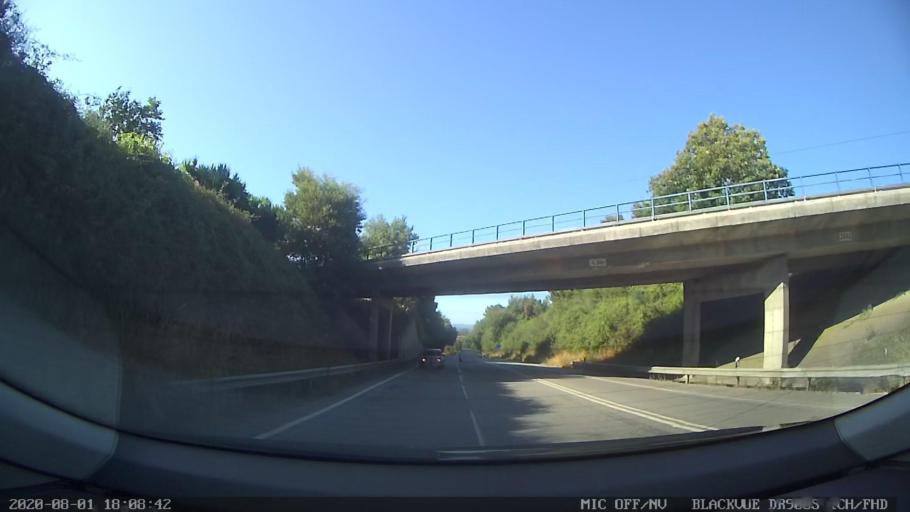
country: PT
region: Porto
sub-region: Santo Tirso
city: Sao Miguel do Couto
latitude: 41.3201
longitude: -8.4692
